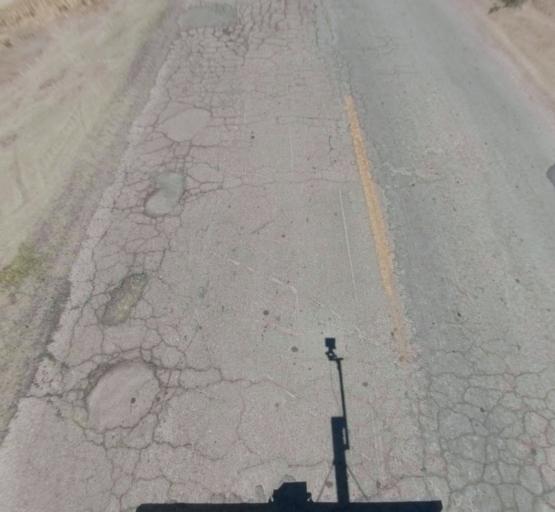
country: US
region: California
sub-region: Merced County
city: Dos Palos
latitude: 37.0546
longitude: -120.4935
